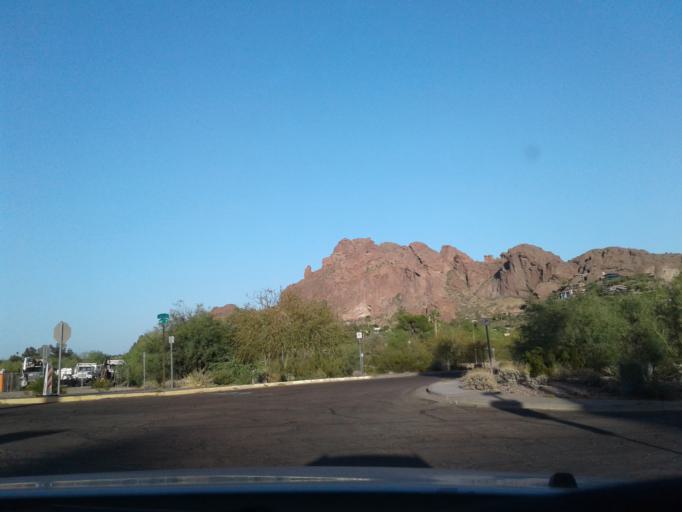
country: US
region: Arizona
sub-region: Maricopa County
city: Paradise Valley
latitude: 33.5237
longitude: -111.9867
